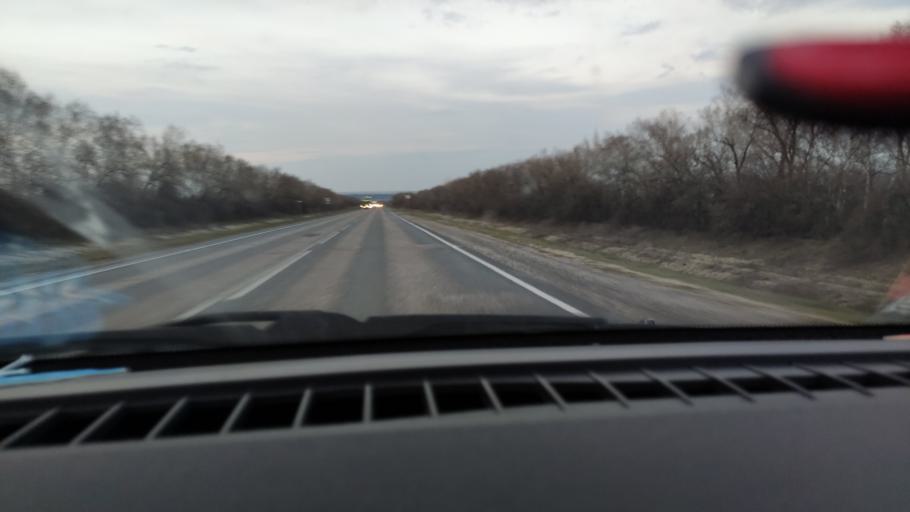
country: RU
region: Saratov
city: Sinodskoye
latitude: 51.9490
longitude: 46.6059
